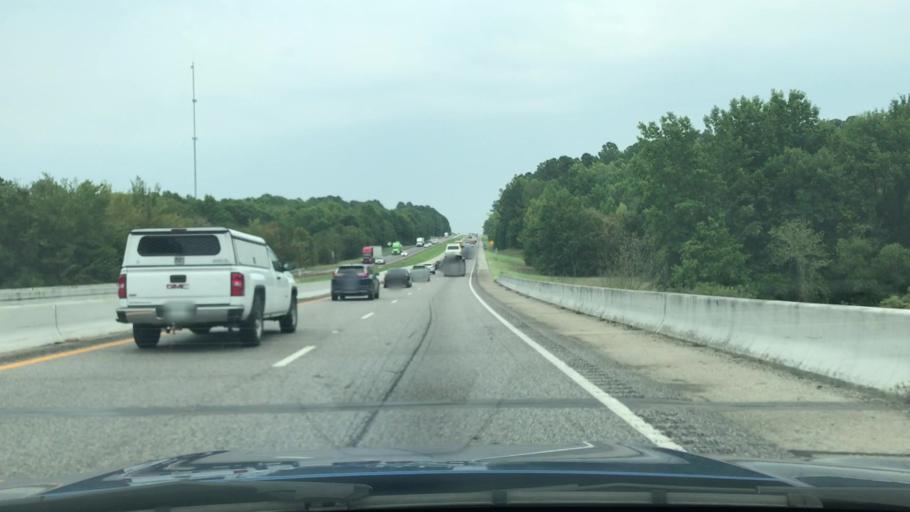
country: US
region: Texas
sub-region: Smith County
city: Lindale
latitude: 32.4675
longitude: -95.3412
